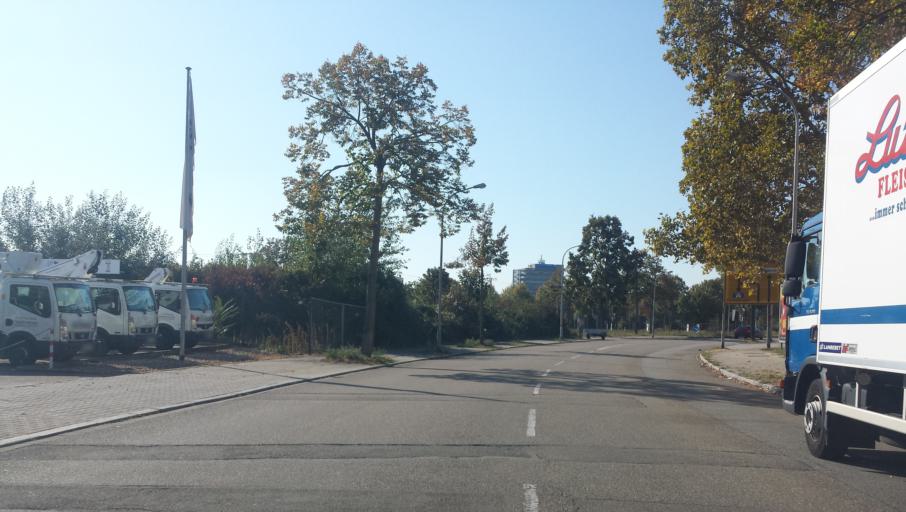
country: DE
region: Baden-Wuerttemberg
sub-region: Karlsruhe Region
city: Mannheim
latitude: 49.4705
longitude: 8.4928
